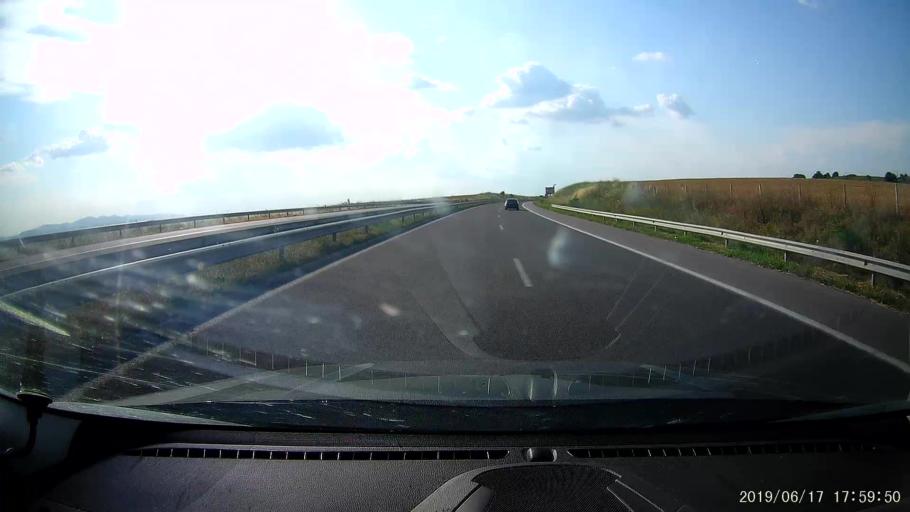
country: BG
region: Khaskovo
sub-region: Obshtina Svilengrad
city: Svilengrad
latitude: 41.7273
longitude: 26.2886
